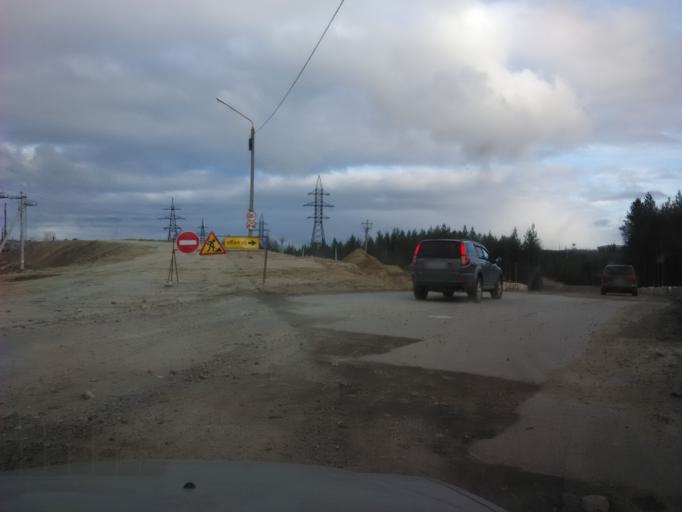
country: RU
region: Murmansk
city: Polyarnyye Zori
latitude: 67.3741
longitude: 32.5077
